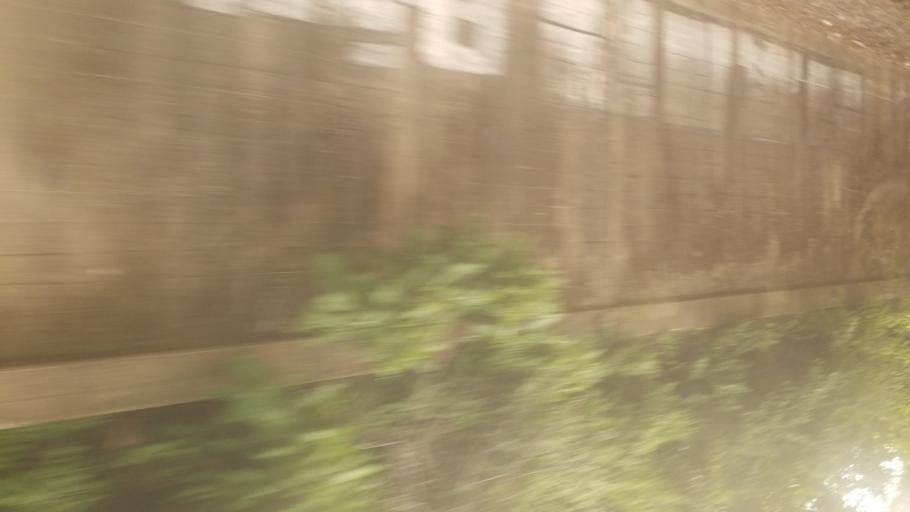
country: US
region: Missouri
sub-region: Jackson County
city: Kansas City
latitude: 39.0884
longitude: -94.5591
